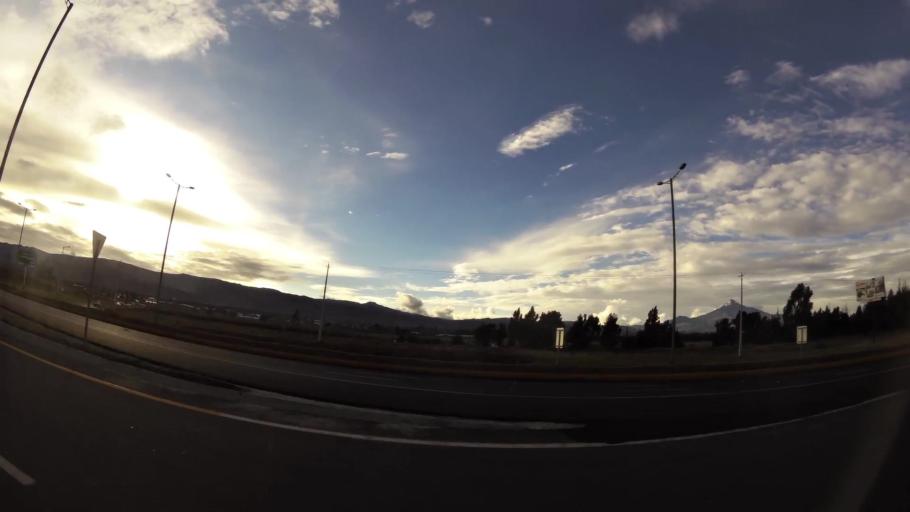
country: EC
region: Cotopaxi
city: Saquisili
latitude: -0.8632
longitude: -78.6246
